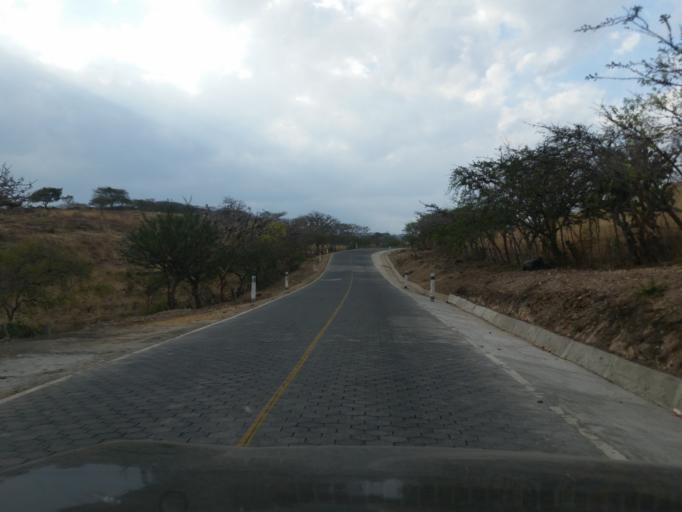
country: NI
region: Jinotega
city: La Concordia
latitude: 13.1880
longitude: -86.1723
